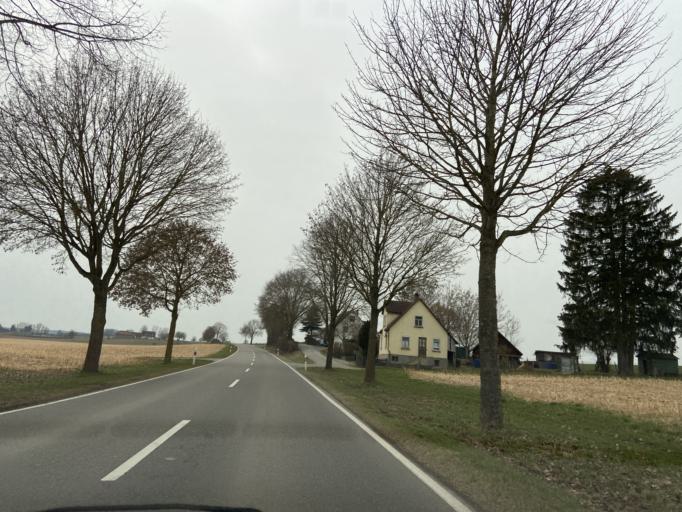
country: DE
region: Baden-Wuerttemberg
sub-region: Tuebingen Region
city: Ostrach
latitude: 47.9421
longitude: 9.3699
